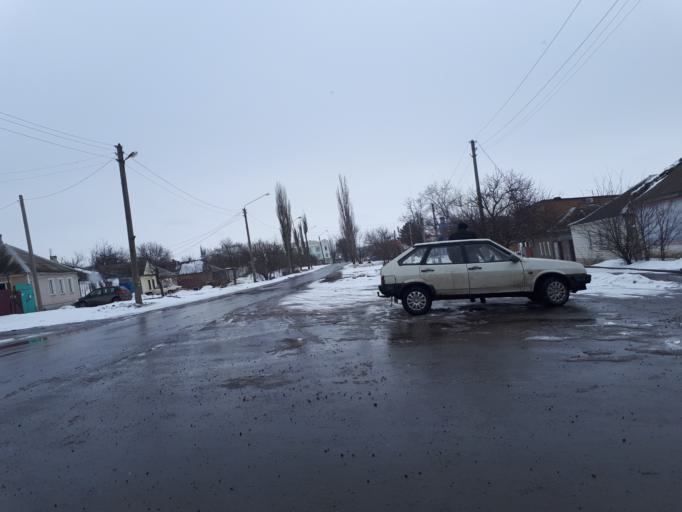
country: RU
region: Rostov
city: Krasnyy Sulin
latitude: 47.8988
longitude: 40.0555
